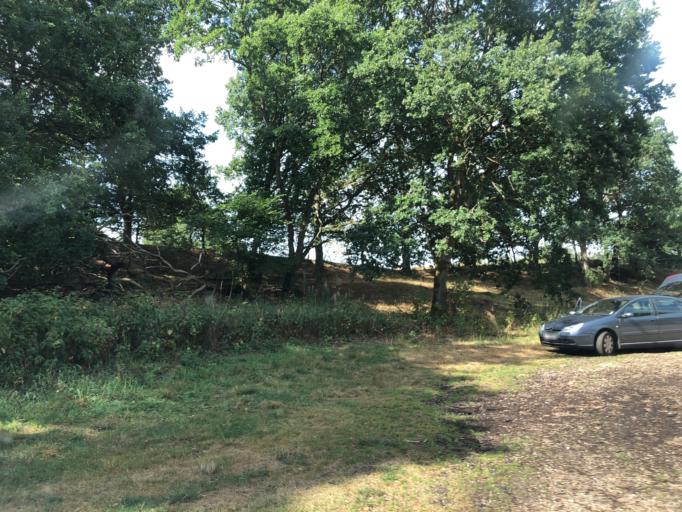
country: DK
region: South Denmark
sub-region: Vejle Kommune
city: Egtved
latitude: 55.6503
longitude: 9.3076
